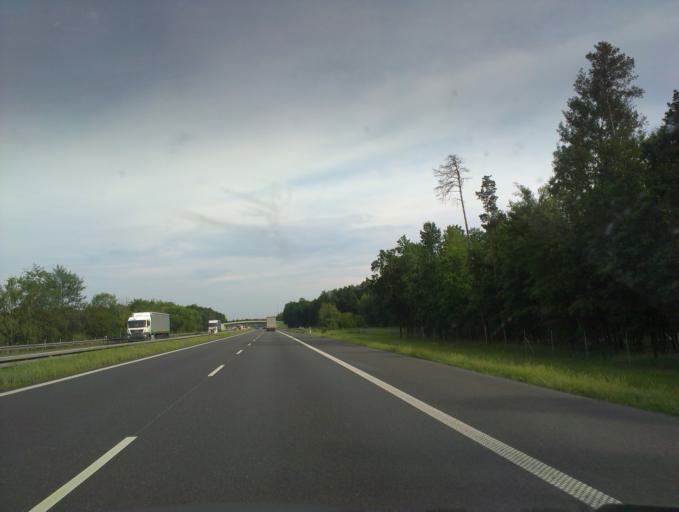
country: PL
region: Opole Voivodeship
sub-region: Powiat opolski
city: Niemodlin
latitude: 50.6895
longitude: 17.6326
